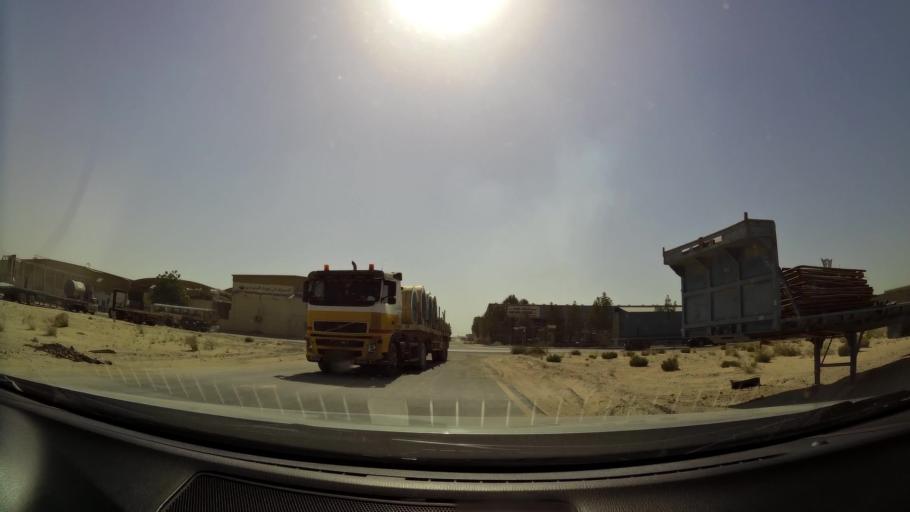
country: AE
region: Dubai
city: Dubai
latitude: 24.9868
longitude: 55.1390
